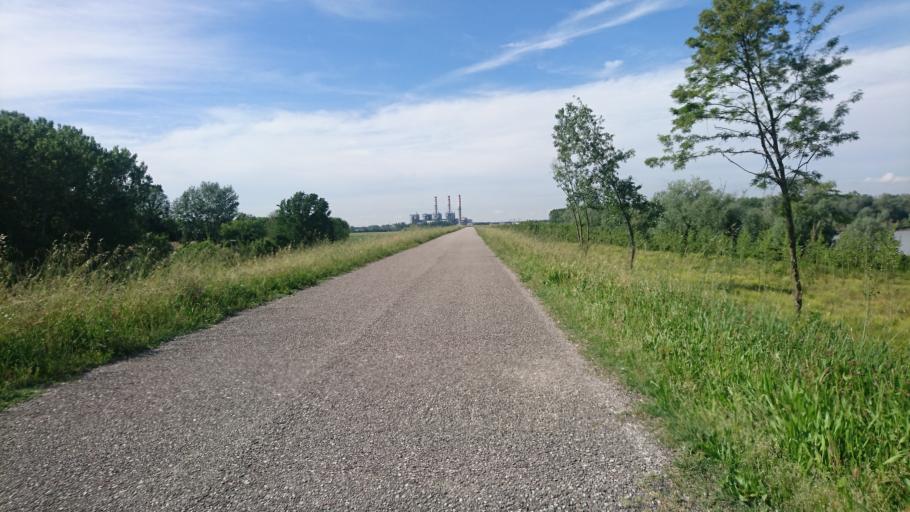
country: IT
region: Veneto
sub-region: Provincia di Rovigo
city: Bergantino
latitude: 45.0463
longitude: 11.2540
